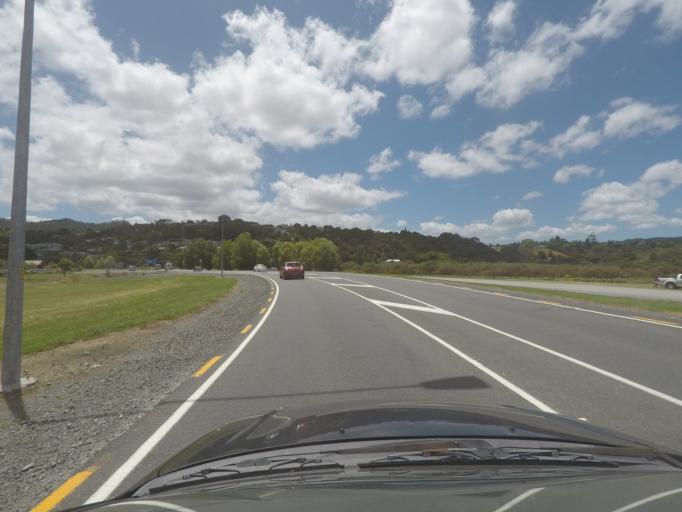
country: NZ
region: Northland
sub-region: Whangarei
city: Whangarei
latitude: -35.7335
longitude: 174.3428
